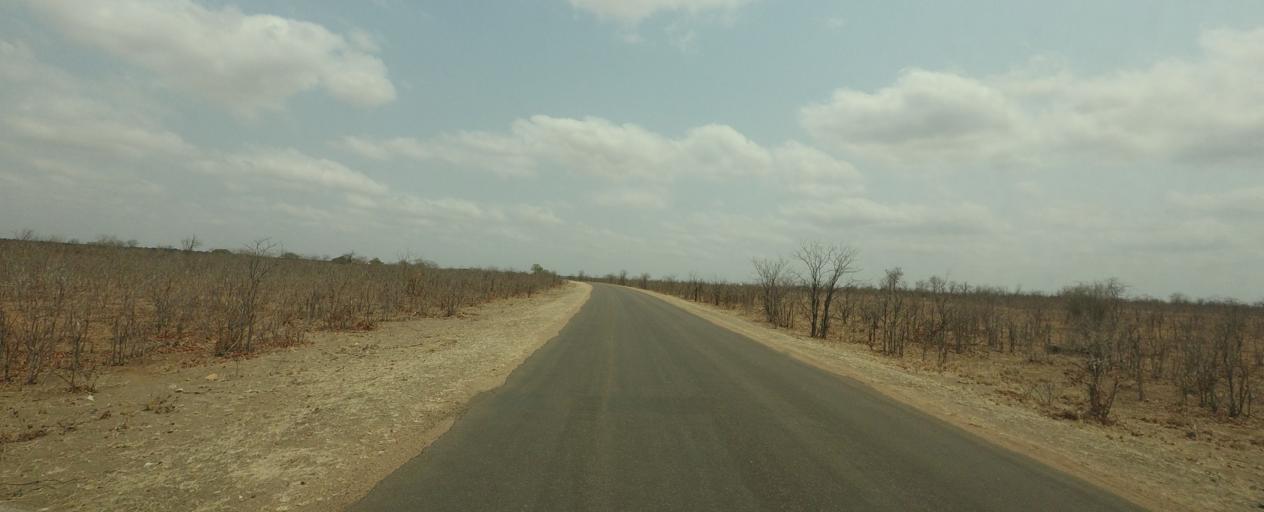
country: ZA
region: Limpopo
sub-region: Mopani District Municipality
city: Phalaborwa
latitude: -23.5531
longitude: 31.4418
